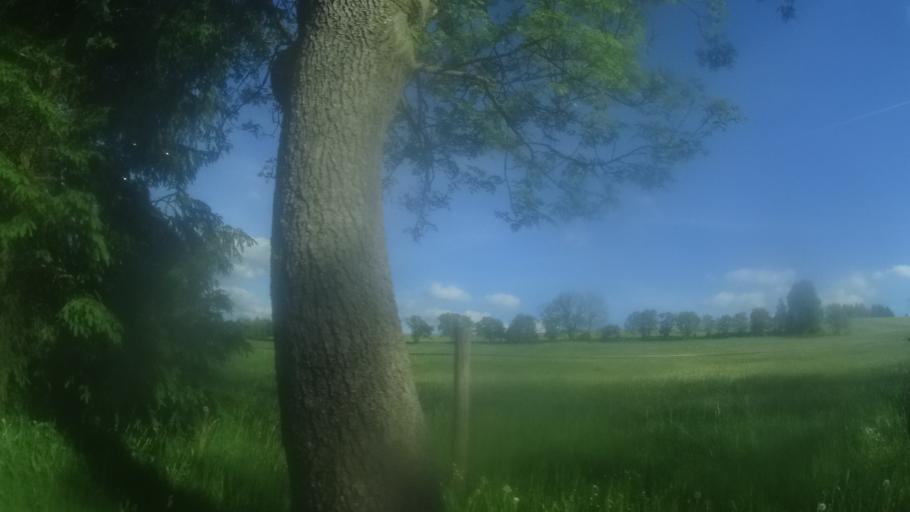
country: DE
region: Thuringia
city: Oberhain
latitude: 50.6339
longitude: 11.1272
